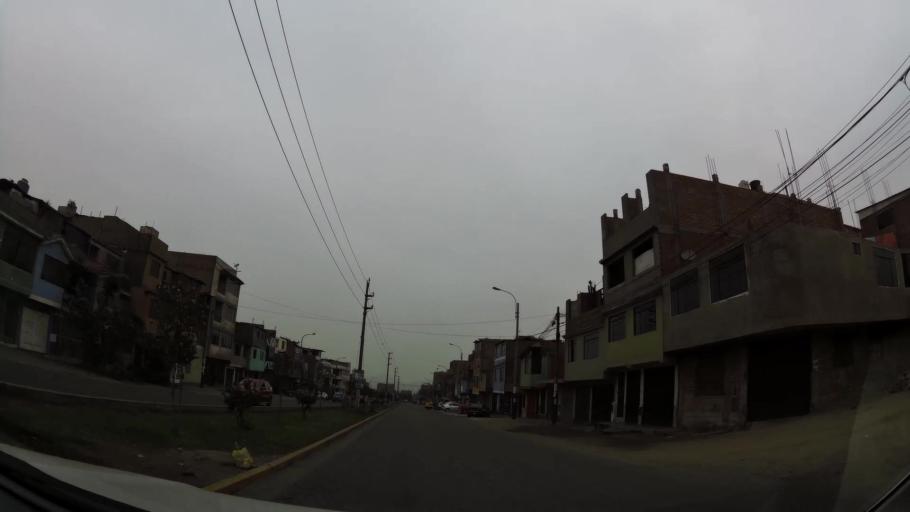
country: PE
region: Lima
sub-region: Lima
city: Independencia
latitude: -11.9572
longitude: -76.9831
